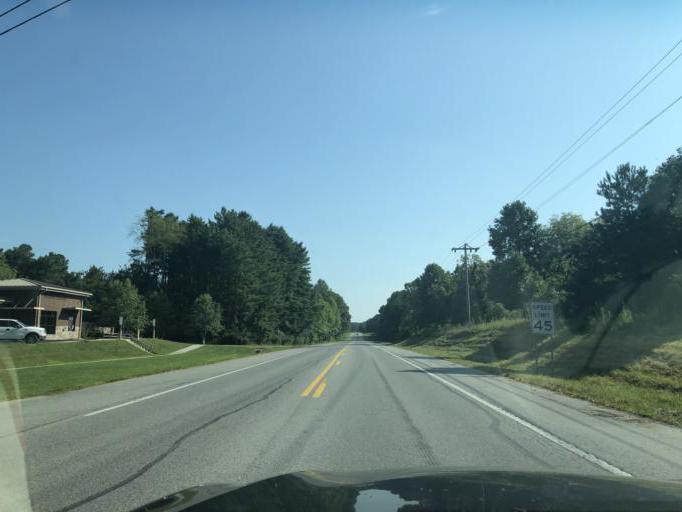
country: US
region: Tennessee
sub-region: Franklin County
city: Sewanee
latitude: 35.1979
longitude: -85.9109
